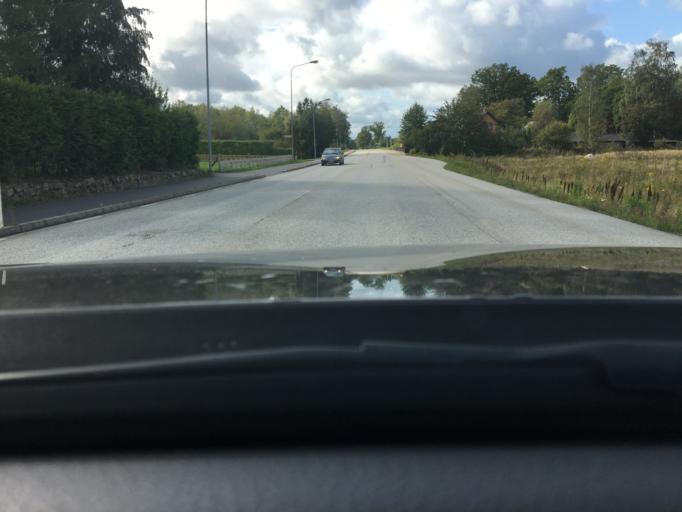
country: SE
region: Skane
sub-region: Horby Kommun
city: Hoerby
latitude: 55.8635
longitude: 13.6893
